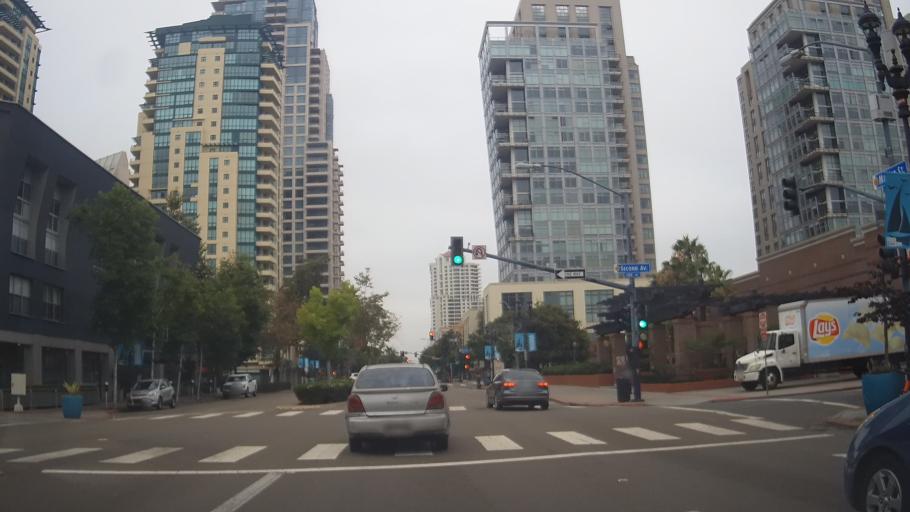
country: US
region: California
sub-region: San Diego County
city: San Diego
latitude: 32.7115
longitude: -117.1627
